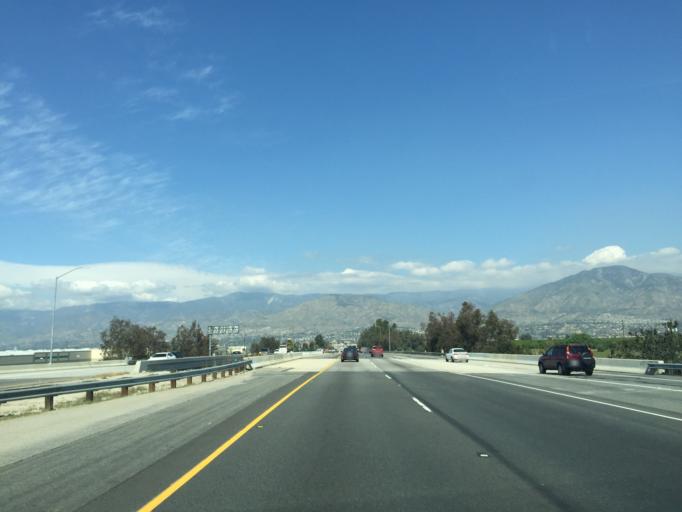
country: US
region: California
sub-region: San Bernardino County
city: Redlands
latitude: 34.0807
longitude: -117.2007
